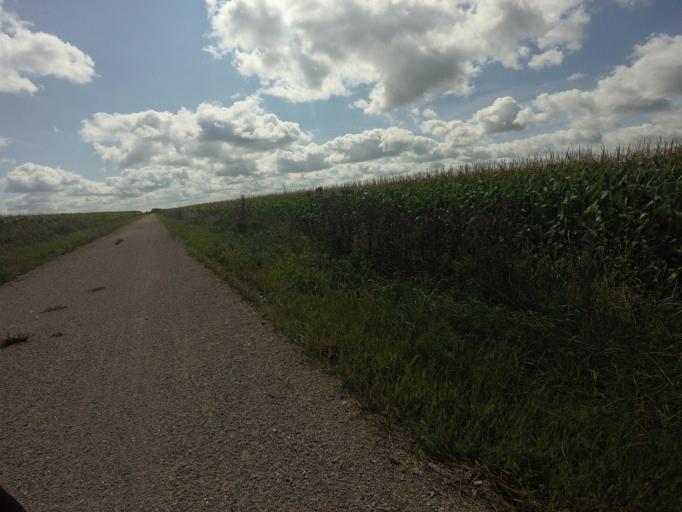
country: CA
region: Ontario
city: Huron East
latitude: 43.6449
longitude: -81.2143
